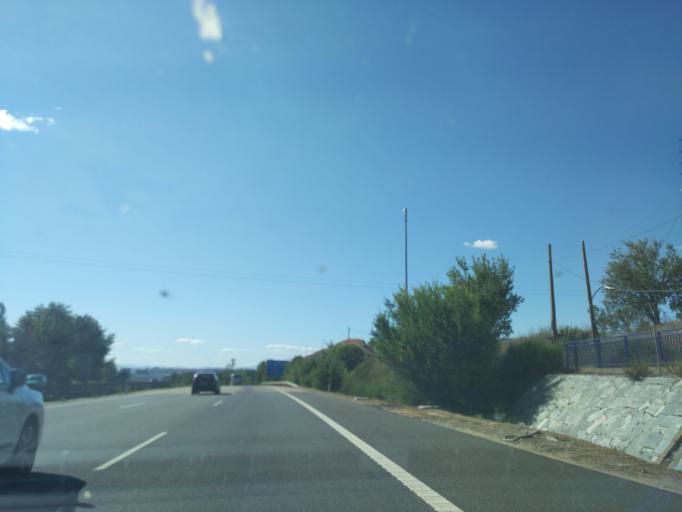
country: ES
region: Castille and Leon
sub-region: Provincia de Zamora
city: Castrogonzalo
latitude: 41.9807
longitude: -5.6154
